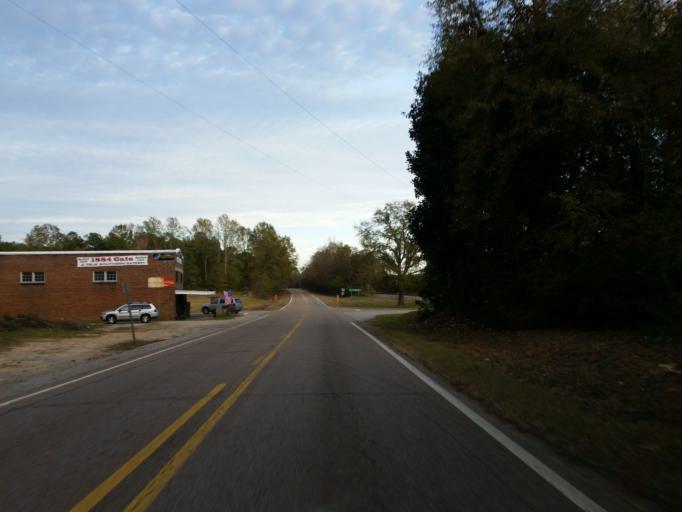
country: US
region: Alabama
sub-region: Sumter County
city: York
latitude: 32.4242
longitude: -88.4391
